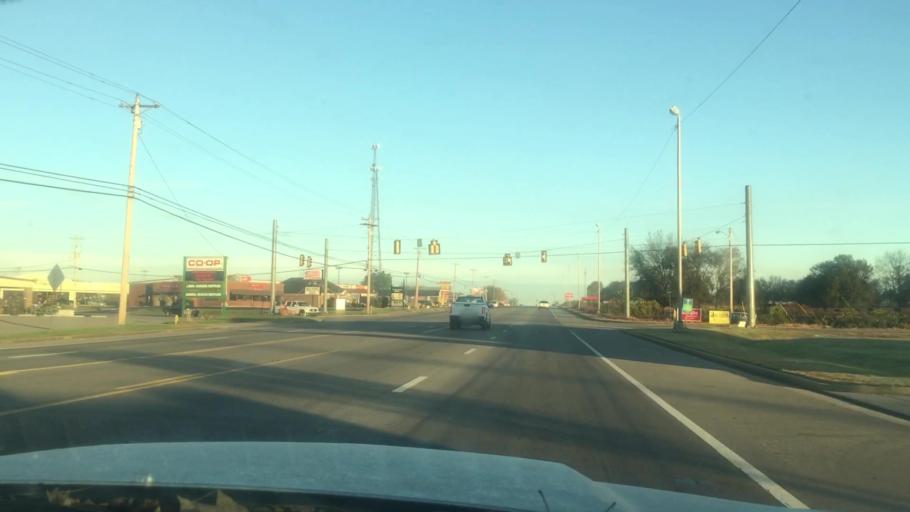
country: US
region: Tennessee
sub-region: Franklin County
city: Decherd
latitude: 35.2118
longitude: -86.0965
